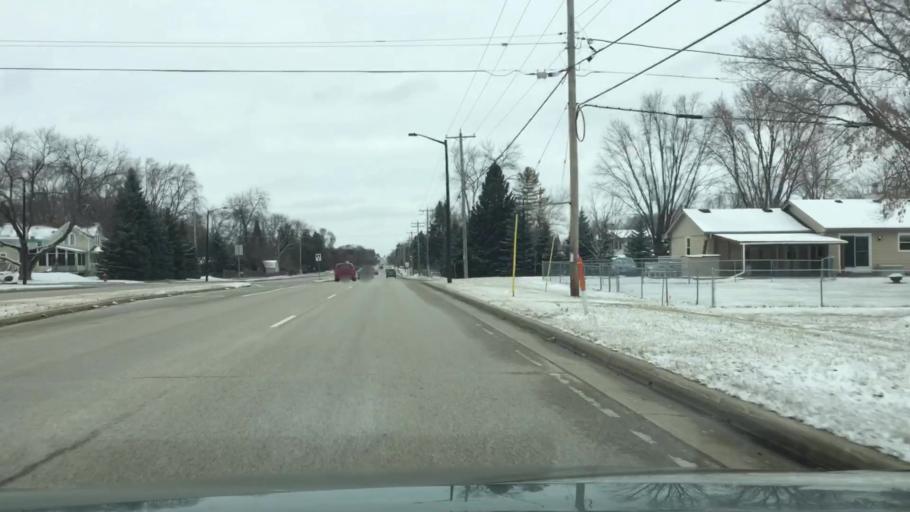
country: US
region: Wisconsin
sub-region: Waukesha County
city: Butler
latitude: 43.1082
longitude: -88.1055
